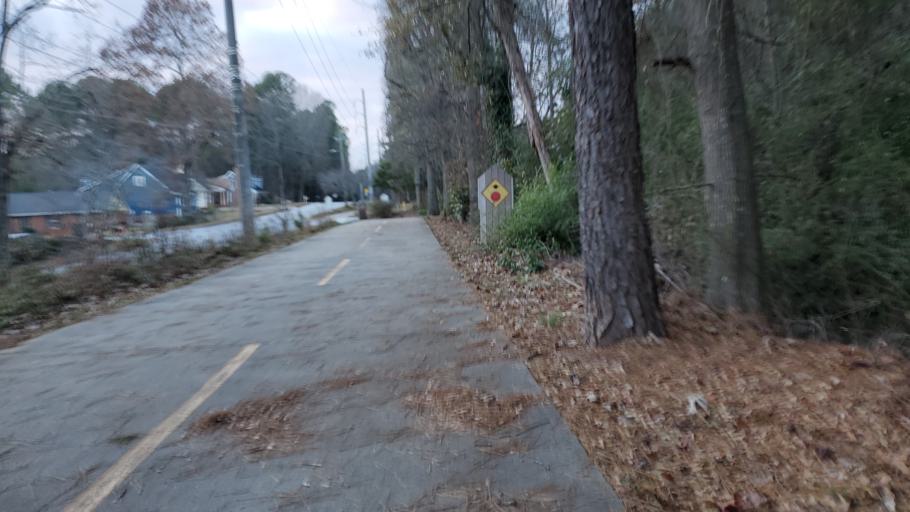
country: US
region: Georgia
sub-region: DeKalb County
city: Clarkston
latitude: 33.8182
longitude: -84.2256
